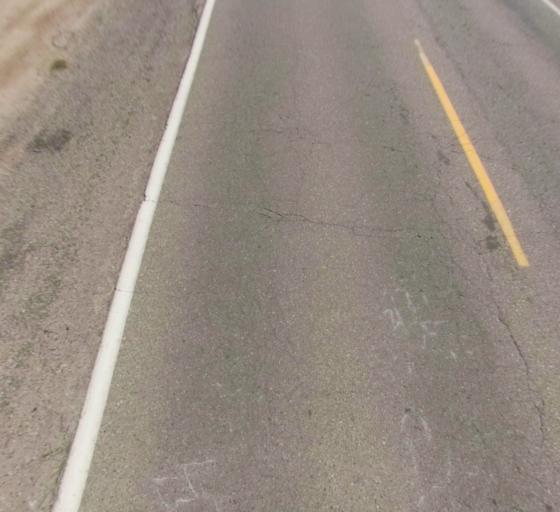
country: US
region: California
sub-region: Fresno County
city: Biola
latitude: 36.8483
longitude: -120.0989
